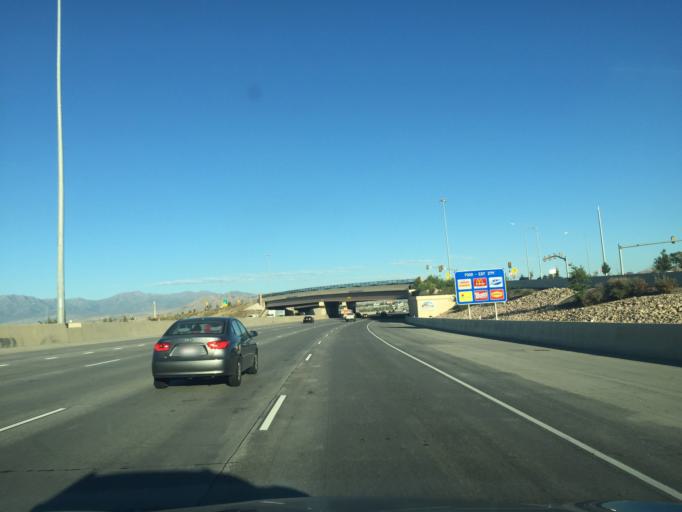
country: US
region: Utah
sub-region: Utah County
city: American Fork
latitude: 40.3757
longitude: -111.8161
